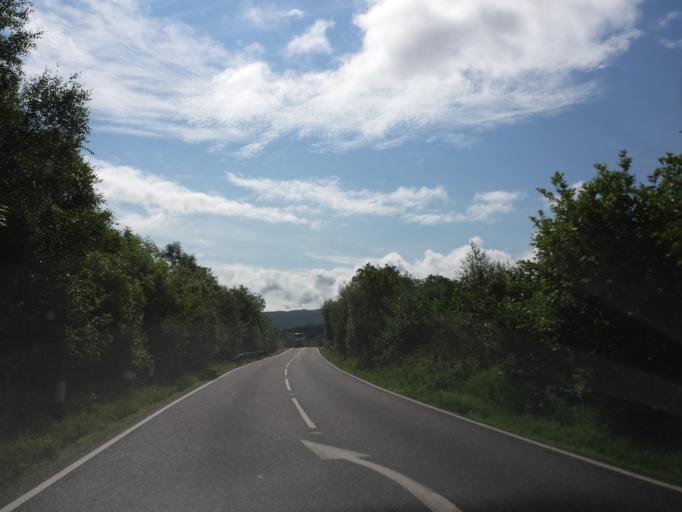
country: GB
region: Scotland
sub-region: Argyll and Bute
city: Garelochhead
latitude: 56.4099
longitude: -5.0218
